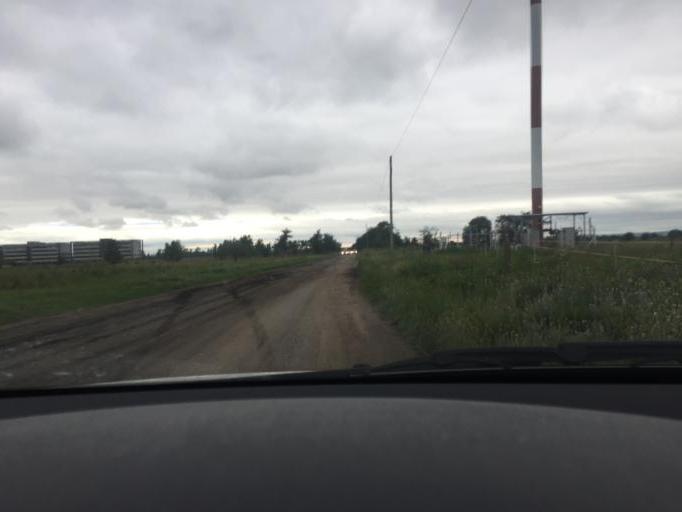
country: AR
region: Cordoba
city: Villa Allende
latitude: -31.3084
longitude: -64.2256
